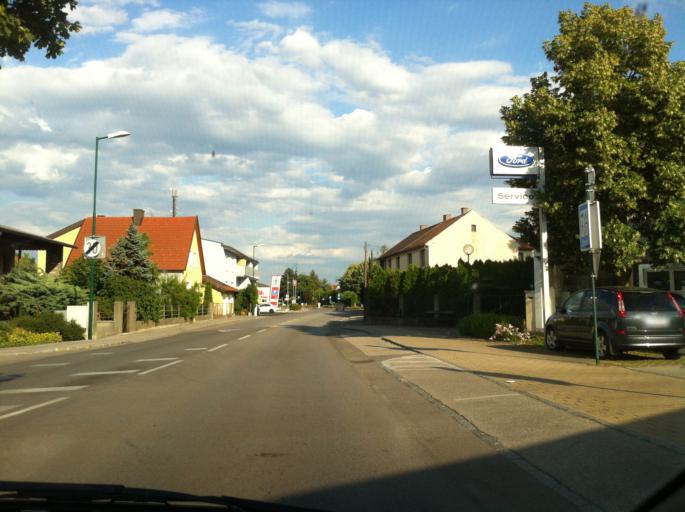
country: AT
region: Lower Austria
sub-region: Politischer Bezirk Tulln
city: Tulln
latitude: 48.3310
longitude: 16.0652
